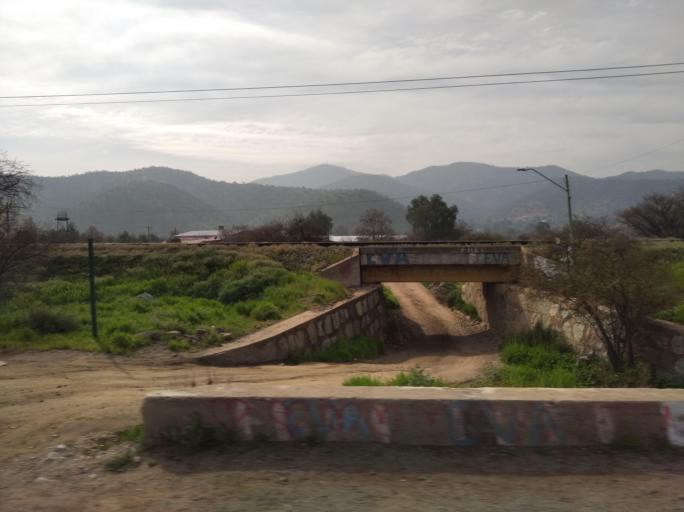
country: CL
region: Santiago Metropolitan
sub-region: Provincia de Chacabuco
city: Lampa
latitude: -33.1102
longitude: -70.9283
